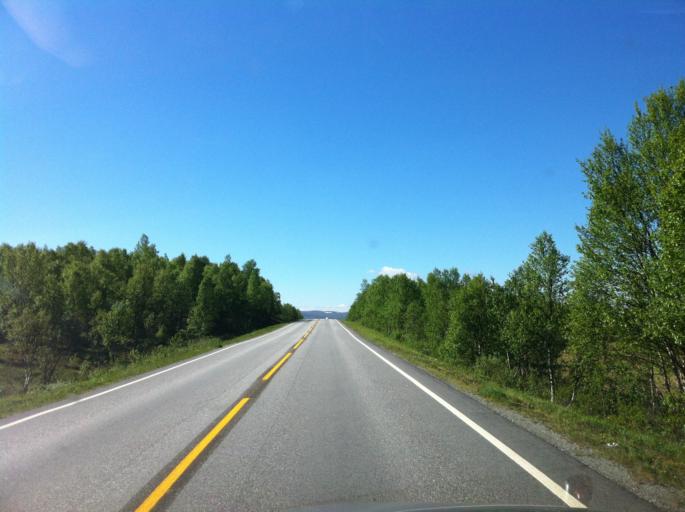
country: NO
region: Sor-Trondelag
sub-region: Tydal
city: Aas
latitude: 62.6411
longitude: 11.8413
